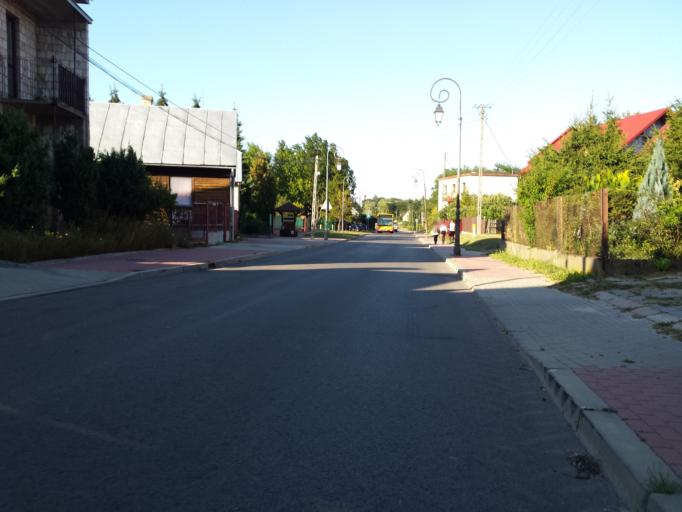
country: PL
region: Swietokrzyskie
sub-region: Powiat kielecki
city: Pierzchnica
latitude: 50.6984
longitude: 20.7562
